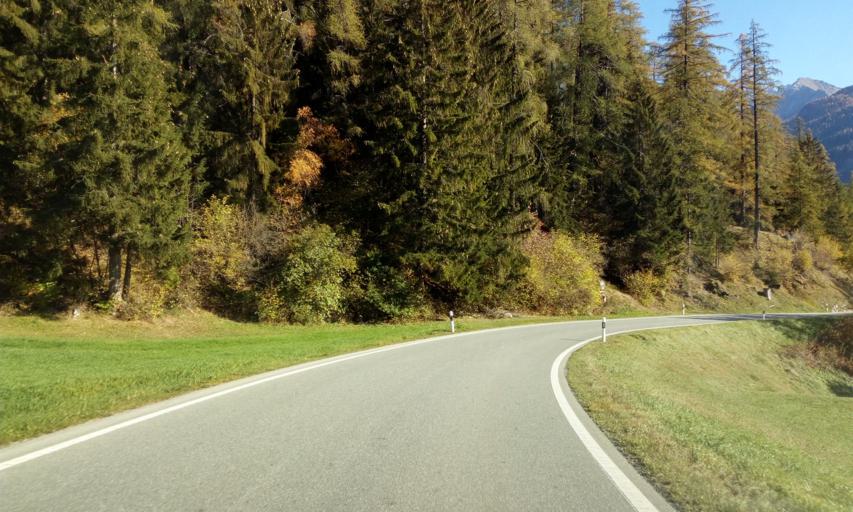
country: CH
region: Grisons
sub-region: Albula District
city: Tiefencastel
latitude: 46.6756
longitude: 9.5779
